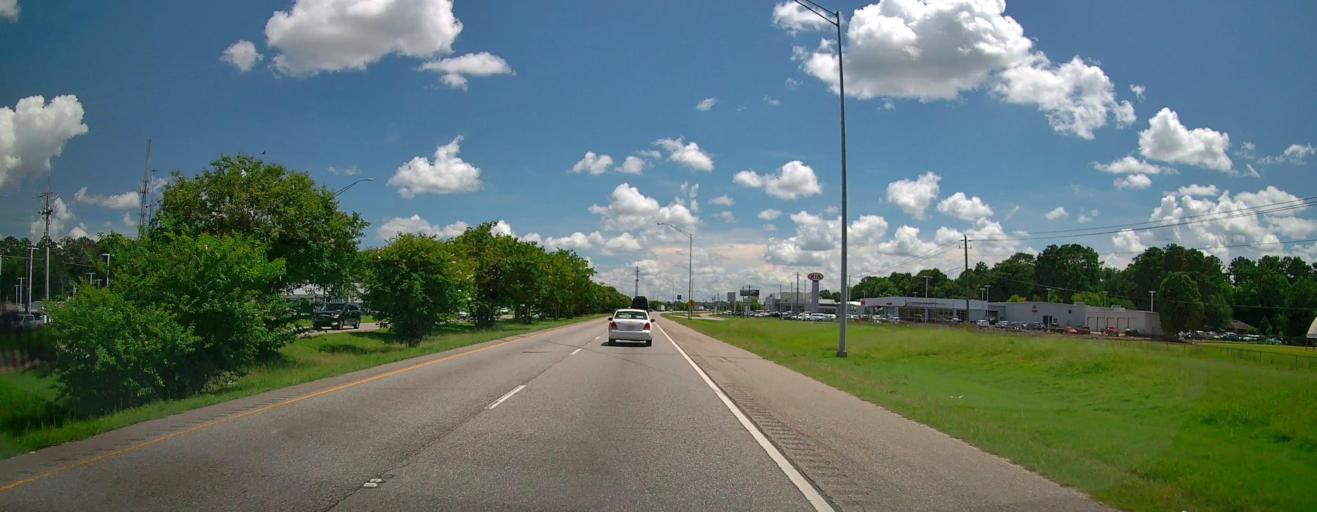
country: US
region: Alabama
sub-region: Montgomery County
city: Montgomery
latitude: 32.3775
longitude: -86.2097
